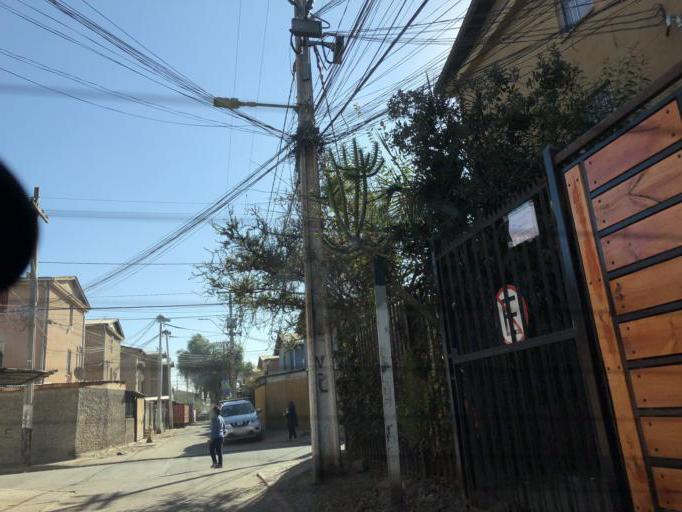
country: CL
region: Santiago Metropolitan
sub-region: Provincia de Cordillera
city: Puente Alto
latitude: -33.6190
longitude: -70.6116
